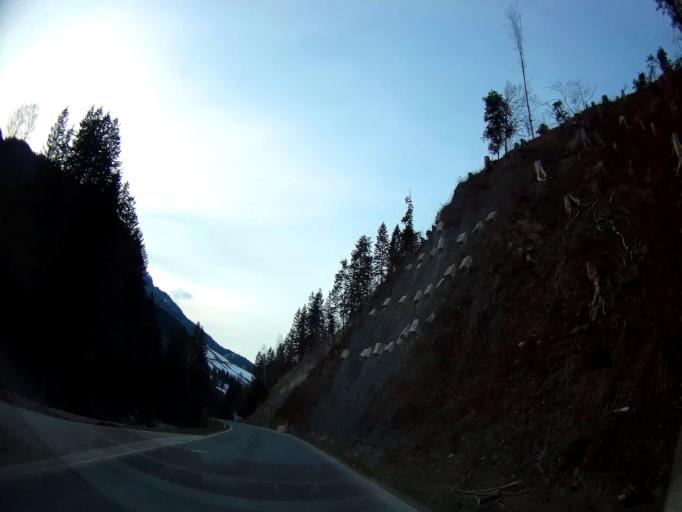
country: AT
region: Salzburg
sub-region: Politischer Bezirk Hallein
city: Abtenau
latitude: 47.5247
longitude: 13.4304
